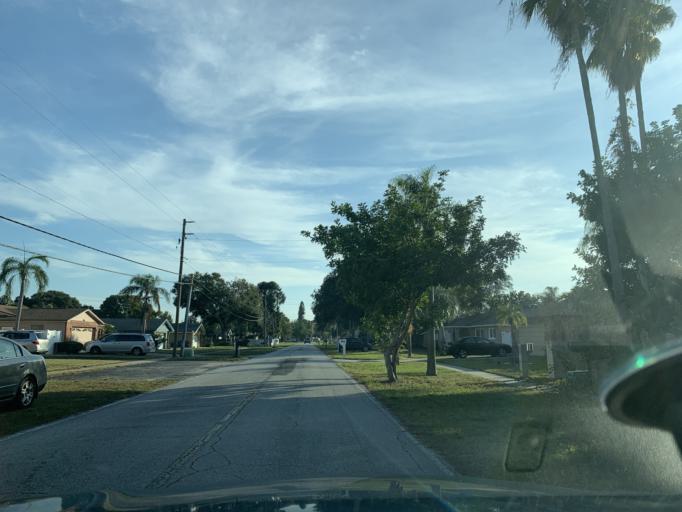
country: US
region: Florida
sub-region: Pinellas County
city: Ridgecrest
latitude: 27.8895
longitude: -82.7974
